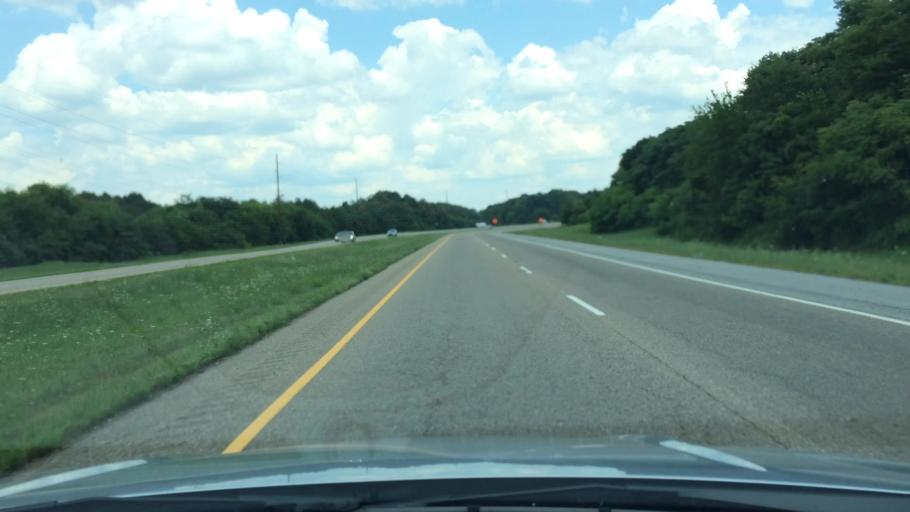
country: US
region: Tennessee
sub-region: Hamblen County
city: Morristown
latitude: 36.1684
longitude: -83.3619
